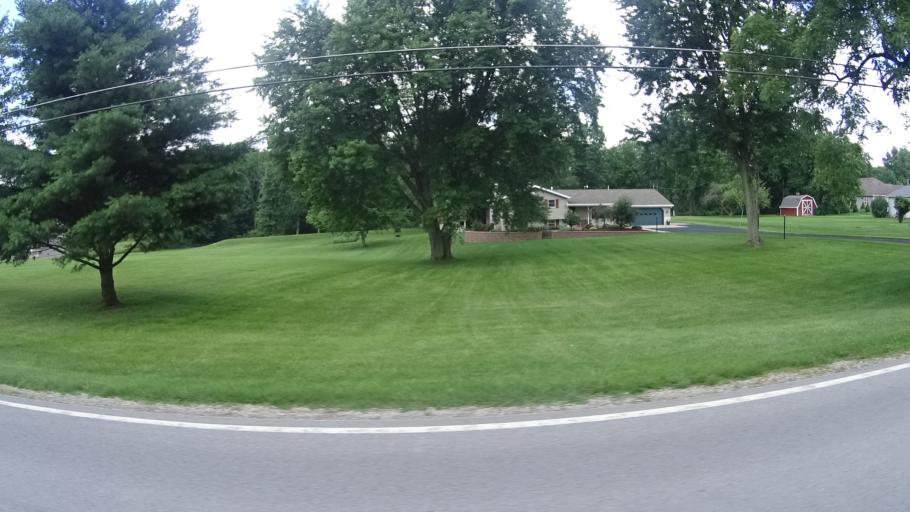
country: US
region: Ohio
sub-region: Huron County
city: Wakeman
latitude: 41.3186
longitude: -82.4137
